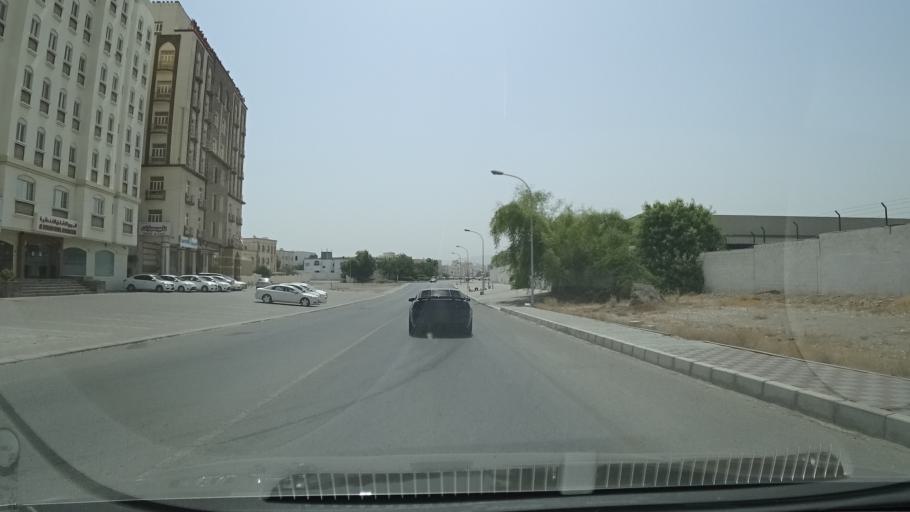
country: OM
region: Muhafazat Masqat
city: Bawshar
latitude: 23.5923
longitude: 58.3735
